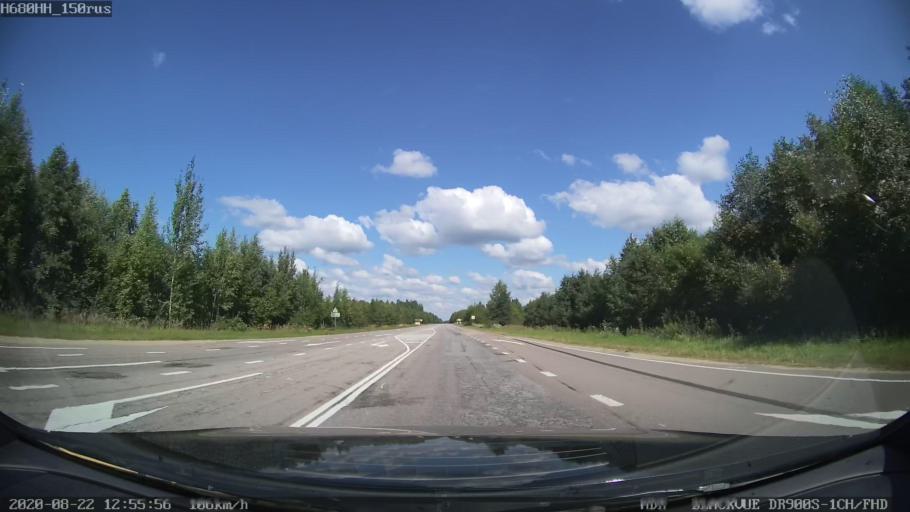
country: RU
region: Tverskaya
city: Rameshki
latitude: 57.5492
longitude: 36.3105
